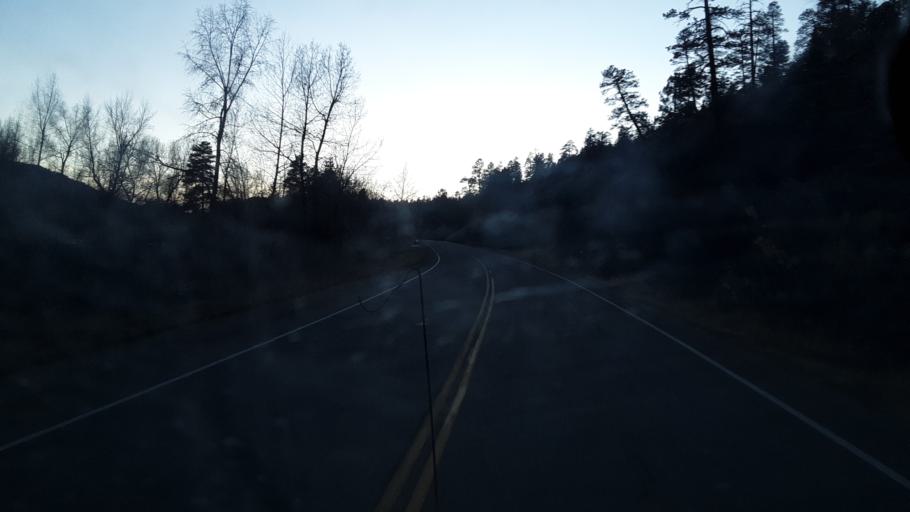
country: US
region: Colorado
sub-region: La Plata County
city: Durango
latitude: 37.3249
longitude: -107.7611
